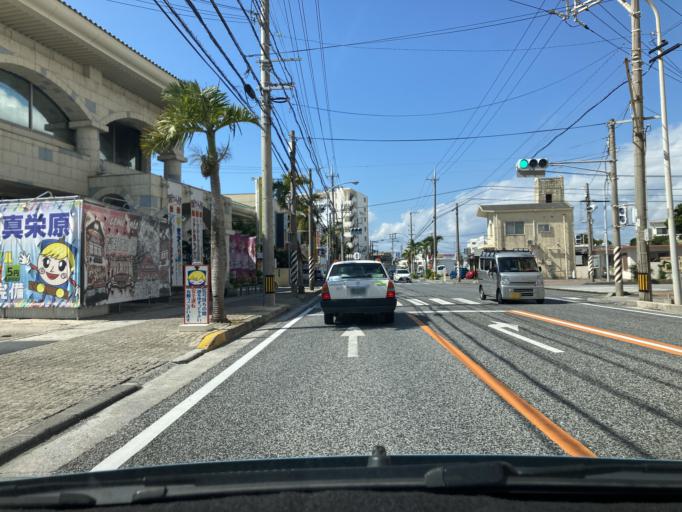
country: JP
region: Okinawa
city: Ginowan
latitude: 26.2624
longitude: 127.7412
